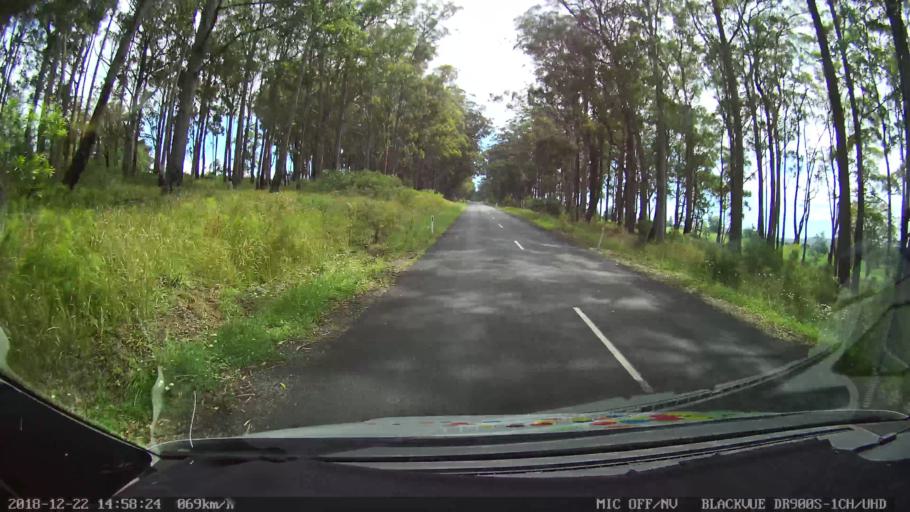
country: AU
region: New South Wales
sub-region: Bellingen
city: Dorrigo
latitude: -30.2399
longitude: 152.4915
